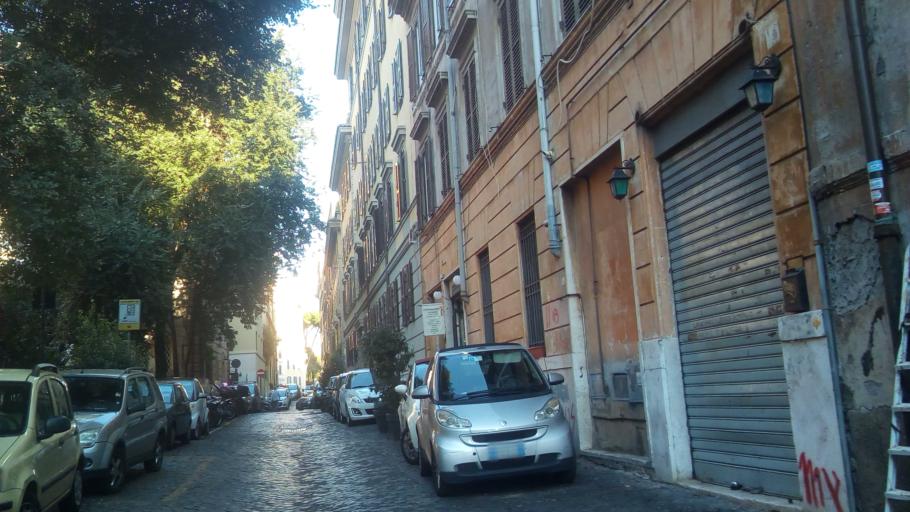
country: VA
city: Vatican City
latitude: 41.9045
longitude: 12.4594
